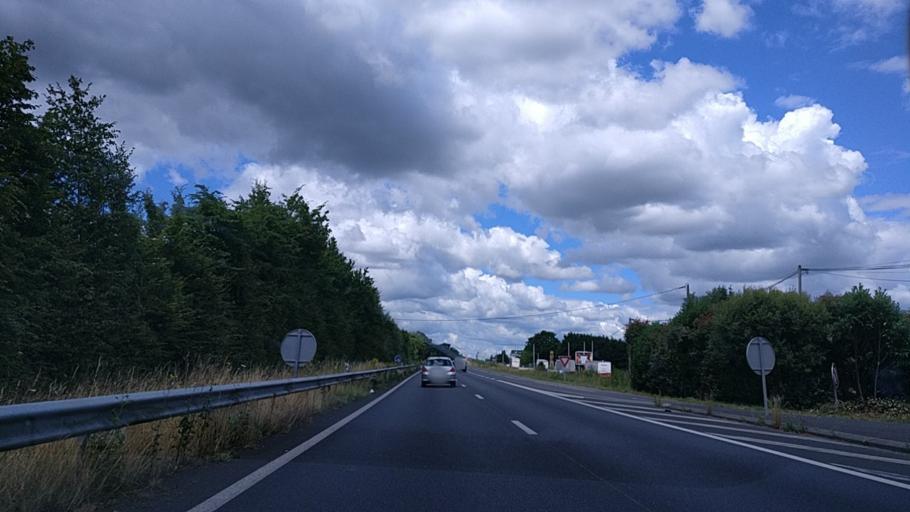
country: FR
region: Pays de la Loire
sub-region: Departement de la Loire-Atlantique
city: Vigneux-de-Bretagne
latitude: 47.2914
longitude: -1.7417
